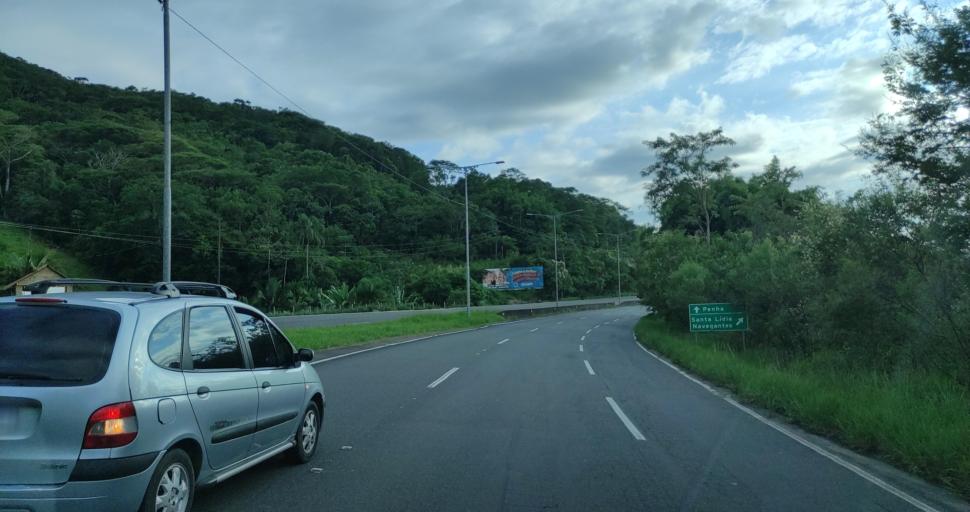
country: BR
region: Santa Catarina
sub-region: Penha
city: Penha
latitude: -26.8058
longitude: -48.6473
